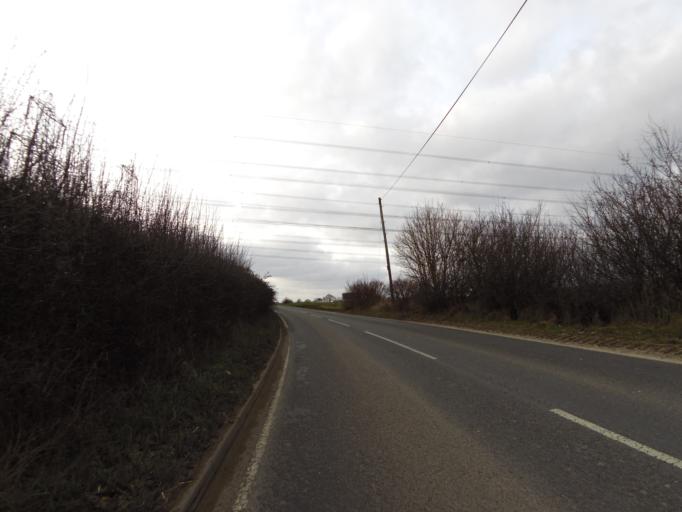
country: GB
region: England
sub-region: Suffolk
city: Ipswich
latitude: 52.0952
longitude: 1.1556
